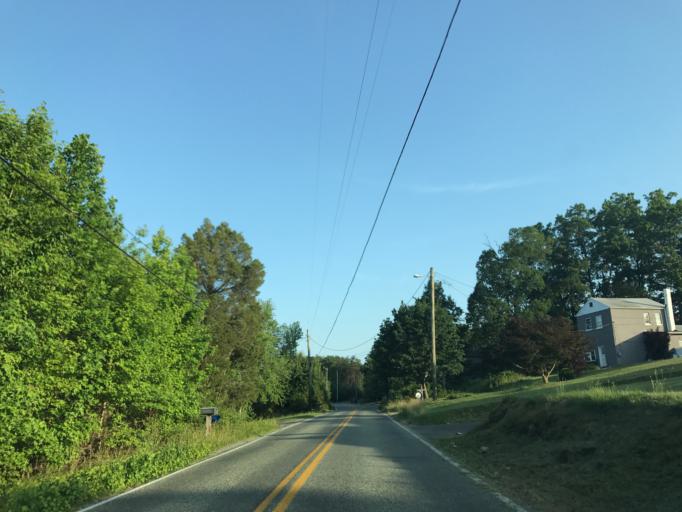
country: US
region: Maryland
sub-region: Harford County
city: Joppatowne
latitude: 39.4174
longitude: -76.3467
